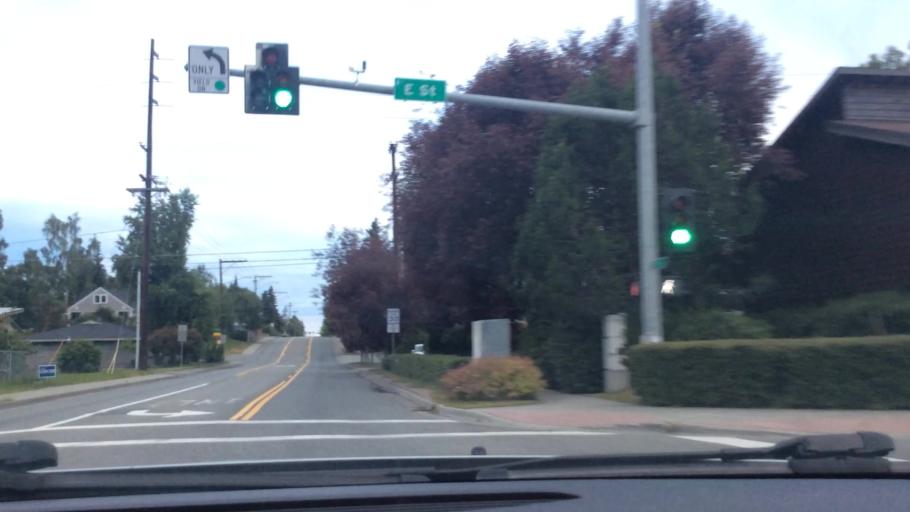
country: US
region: Alaska
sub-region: Anchorage Municipality
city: Anchorage
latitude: 61.2077
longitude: -149.8913
